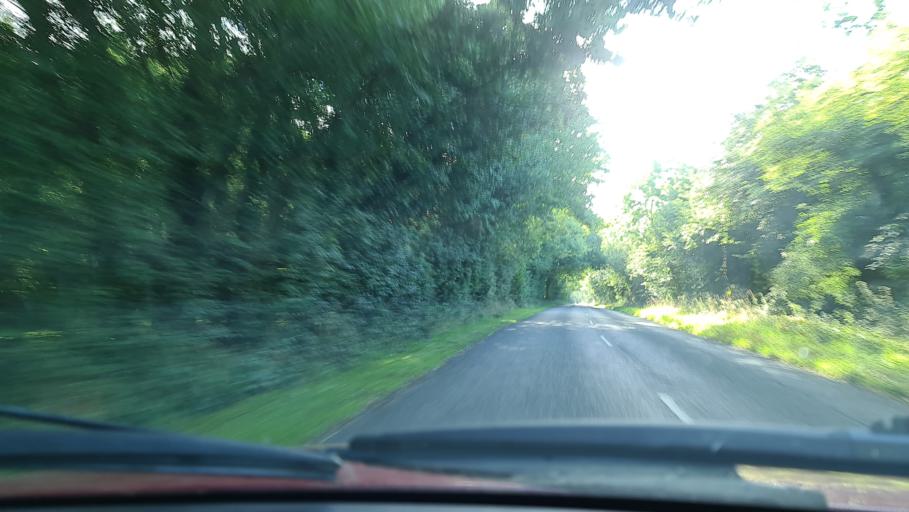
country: GB
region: England
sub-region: Buckinghamshire
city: Stokenchurch
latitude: 51.6878
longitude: -0.8783
